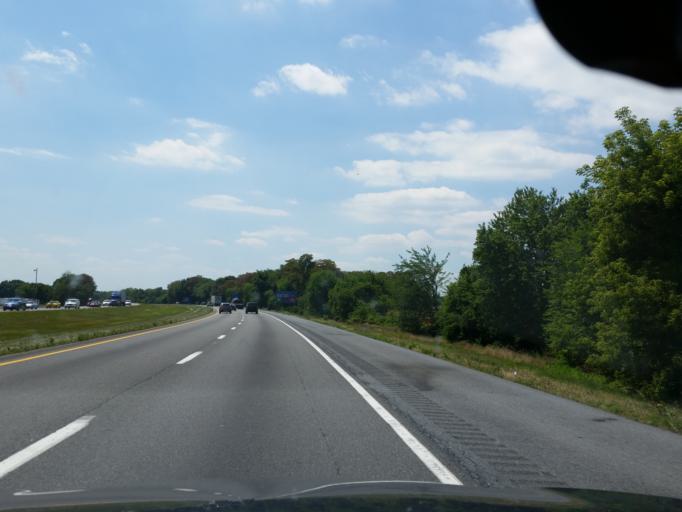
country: US
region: Pennsylvania
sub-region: Cumberland County
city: Schlusser
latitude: 40.2423
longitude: -77.1146
